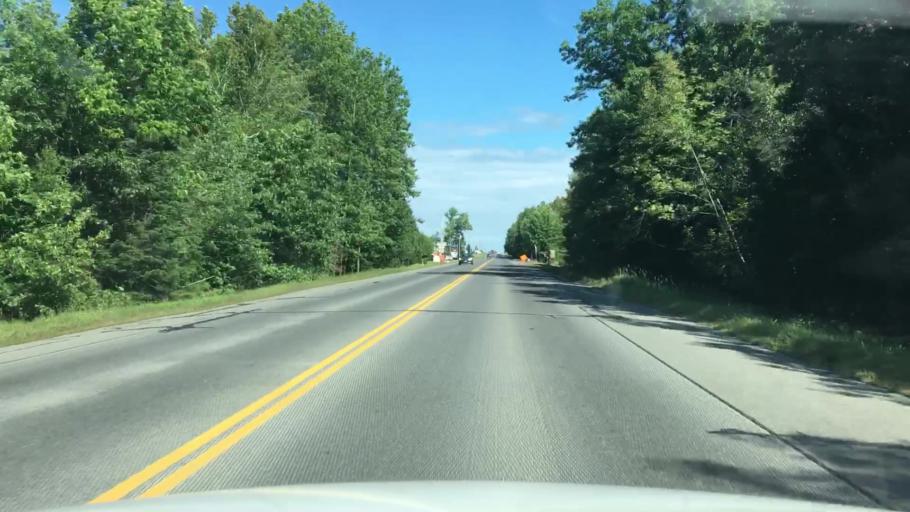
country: US
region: Maine
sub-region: Penobscot County
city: Newport
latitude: 44.8684
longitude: -69.2834
